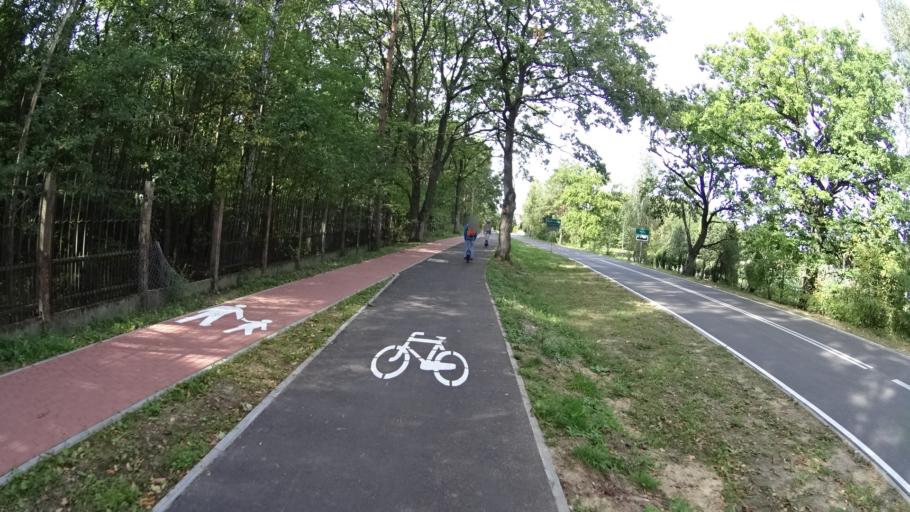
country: PL
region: Masovian Voivodeship
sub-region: Powiat legionowski
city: Bialobrzegi
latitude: 52.4696
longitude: 21.0735
